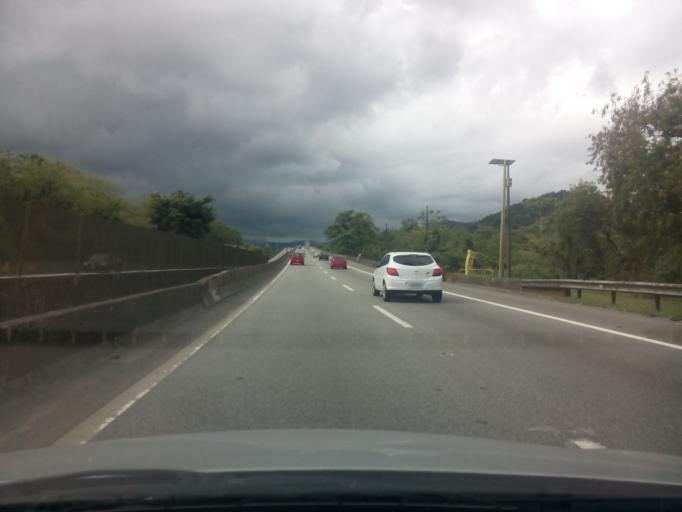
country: BR
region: Sao Paulo
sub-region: Santos
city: Santos
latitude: -23.9269
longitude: -46.2853
